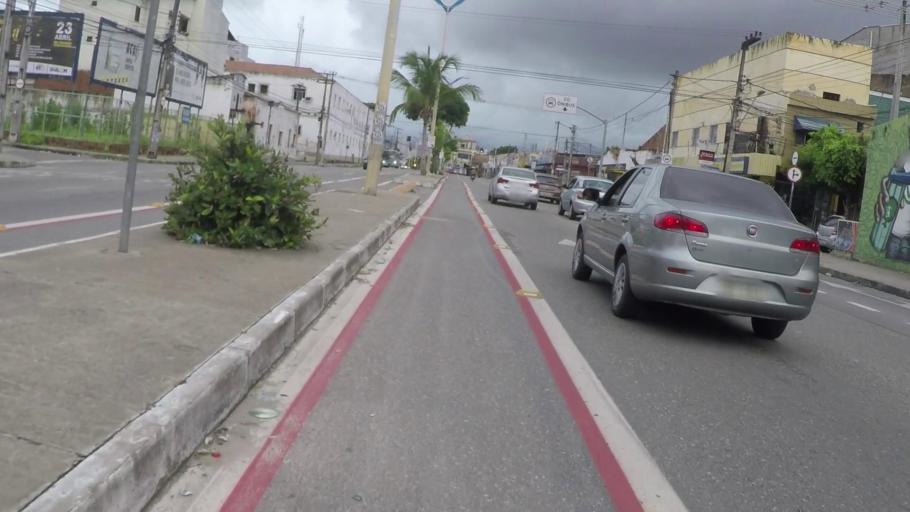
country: BR
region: Ceara
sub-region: Fortaleza
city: Fortaleza
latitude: -3.7370
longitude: -38.5309
